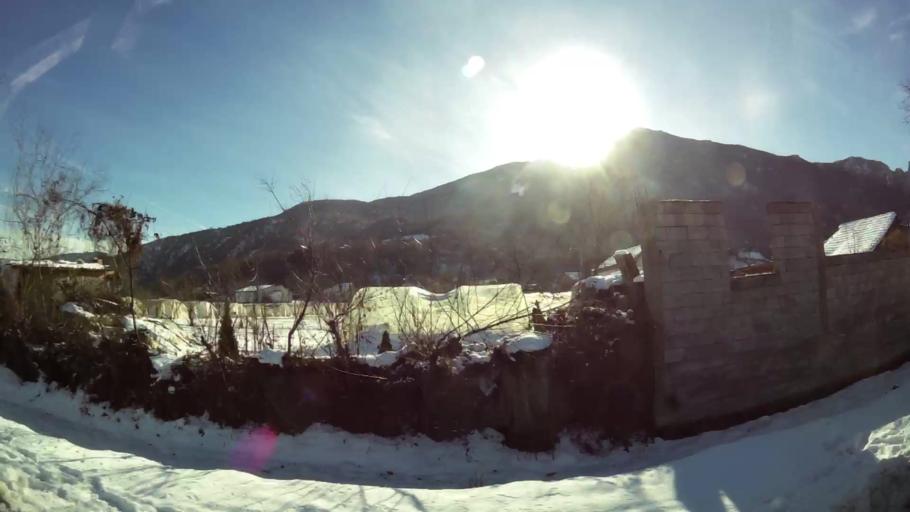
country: MK
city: Grchec
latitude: 41.9761
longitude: 21.3121
